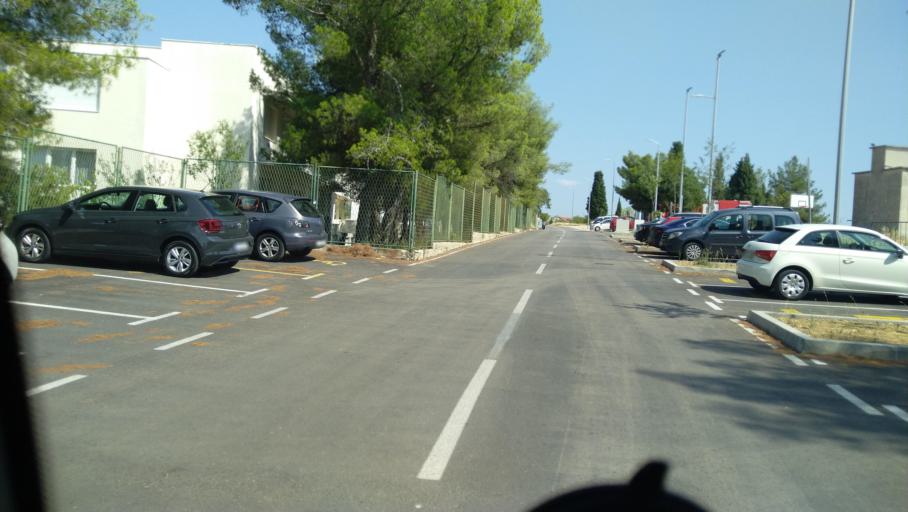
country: HR
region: Sibensko-Kniniska
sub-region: Grad Sibenik
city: Sibenik
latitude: 43.7169
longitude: 15.9077
